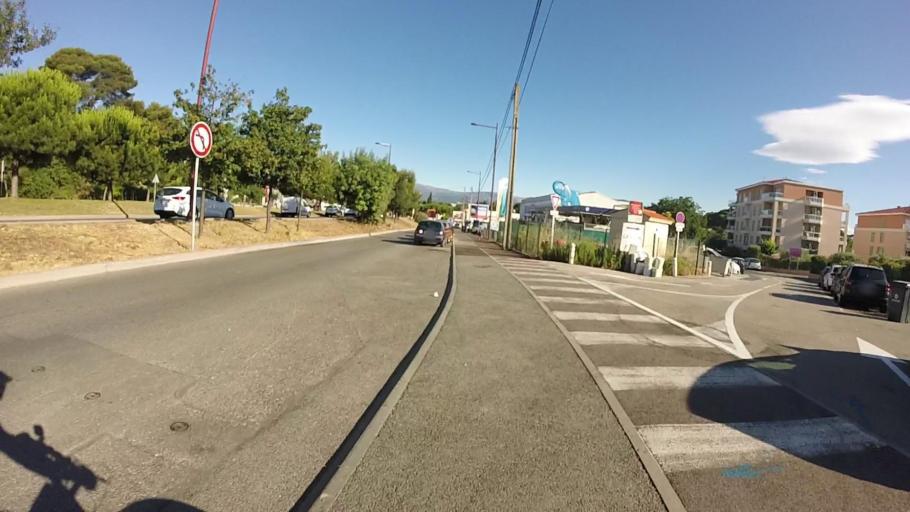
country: FR
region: Provence-Alpes-Cote d'Azur
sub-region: Departement des Alpes-Maritimes
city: Biot
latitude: 43.5968
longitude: 7.0901
